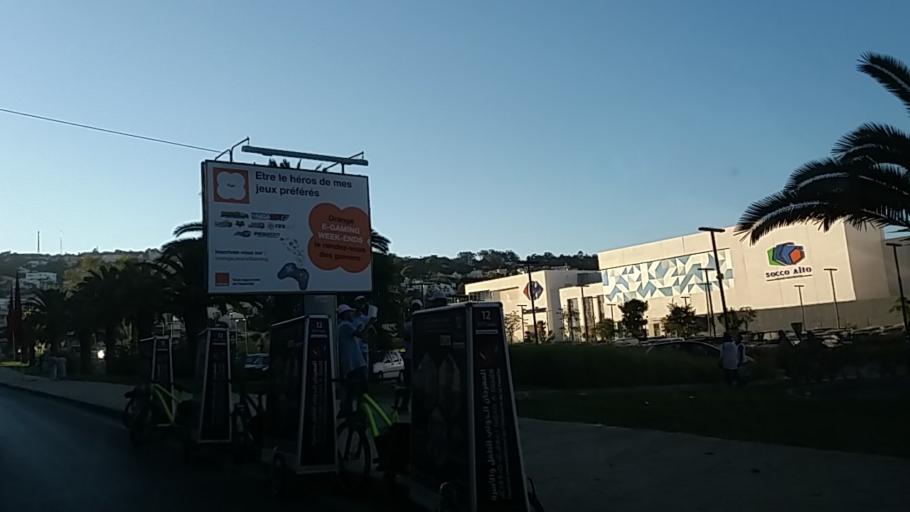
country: MA
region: Tanger-Tetouan
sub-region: Tanger-Assilah
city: Tangier
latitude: 35.7800
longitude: -5.8409
